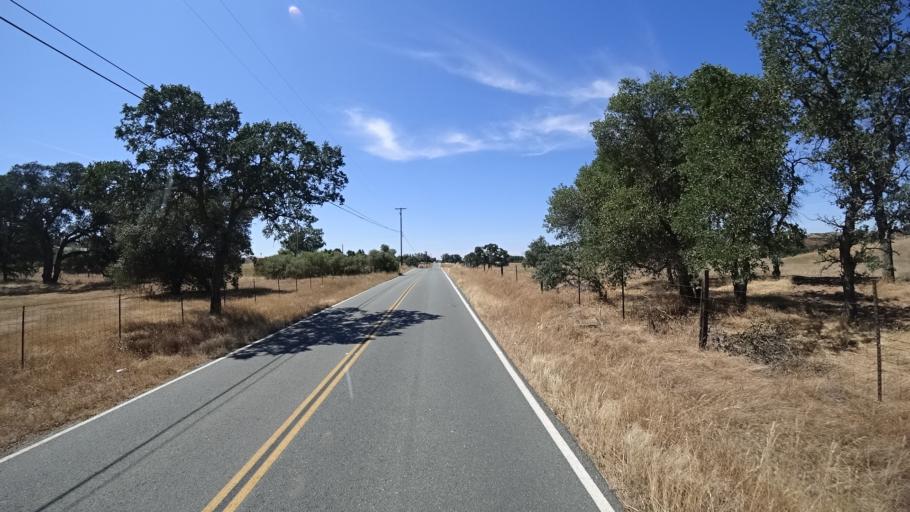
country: US
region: California
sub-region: Calaveras County
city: Rancho Calaveras
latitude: 38.1574
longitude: -120.9180
